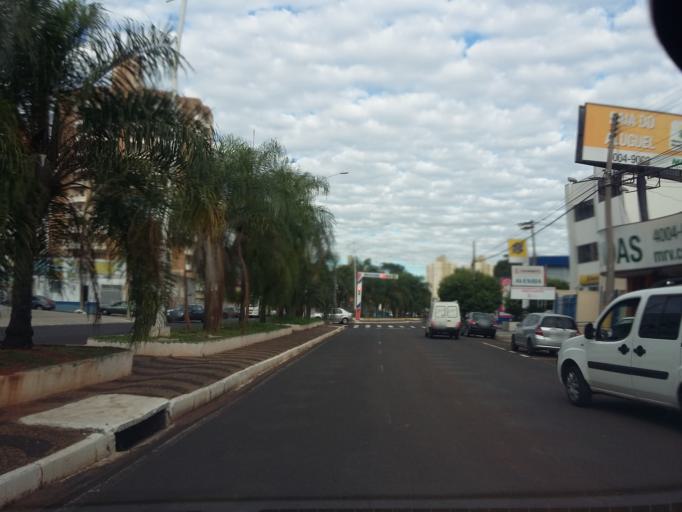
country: BR
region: Sao Paulo
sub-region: Sao Jose Do Rio Preto
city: Sao Jose do Rio Preto
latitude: -20.8120
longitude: -49.3874
